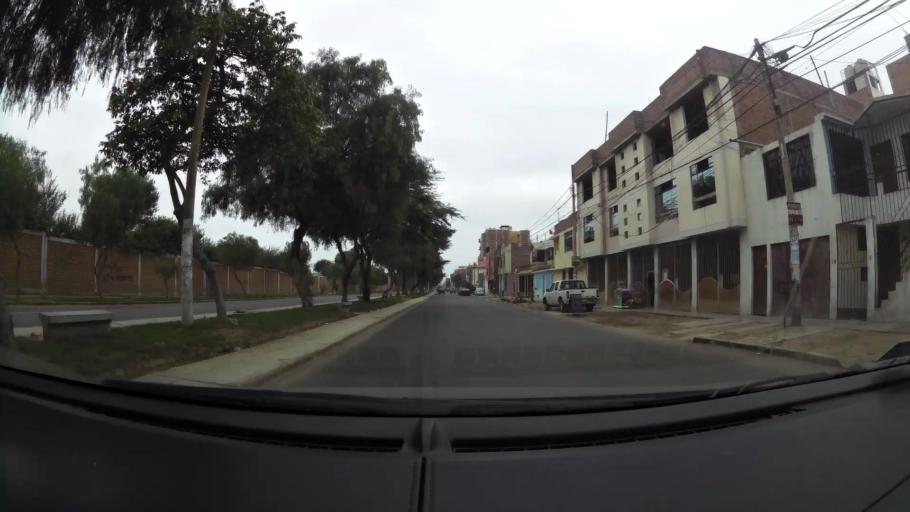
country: PE
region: La Libertad
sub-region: Provincia de Trujillo
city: Trujillo
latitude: -8.1137
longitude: -79.0418
